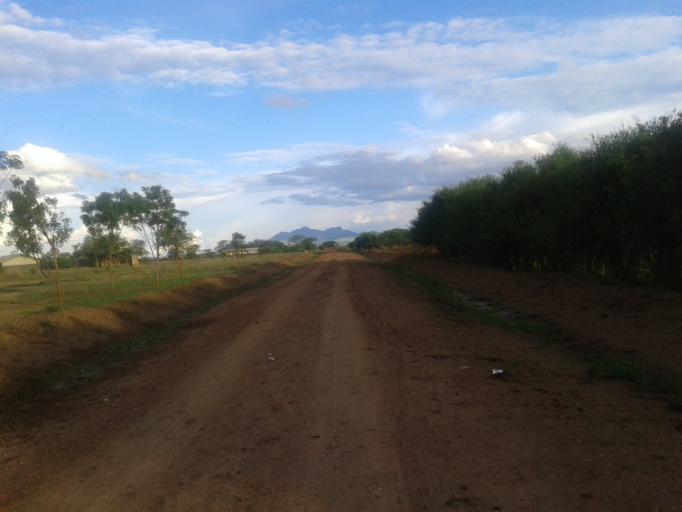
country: UG
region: Northern Region
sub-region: Kotido District
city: Kotido
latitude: 2.9971
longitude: 34.1042
